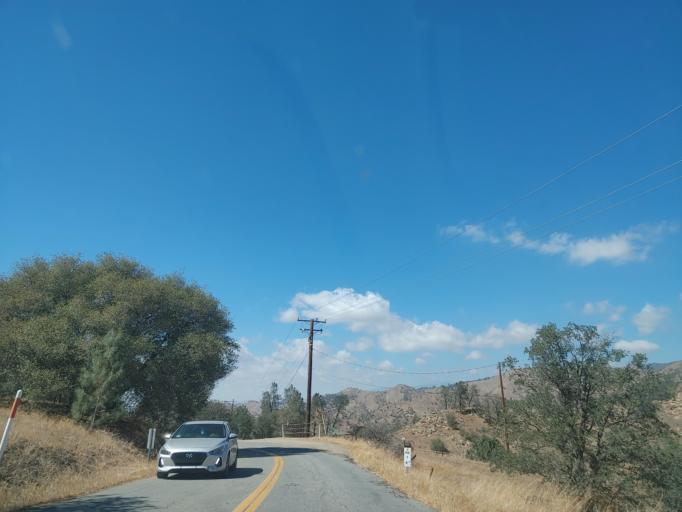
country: US
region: California
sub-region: Kern County
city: Golden Hills
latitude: 35.1898
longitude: -118.5218
